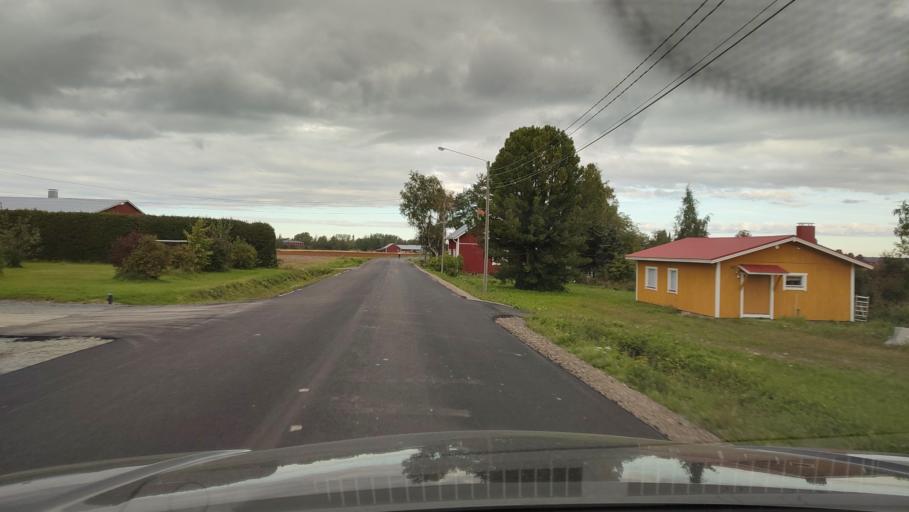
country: FI
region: Southern Ostrobothnia
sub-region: Suupohja
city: Karijoki
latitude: 62.2435
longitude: 21.5611
